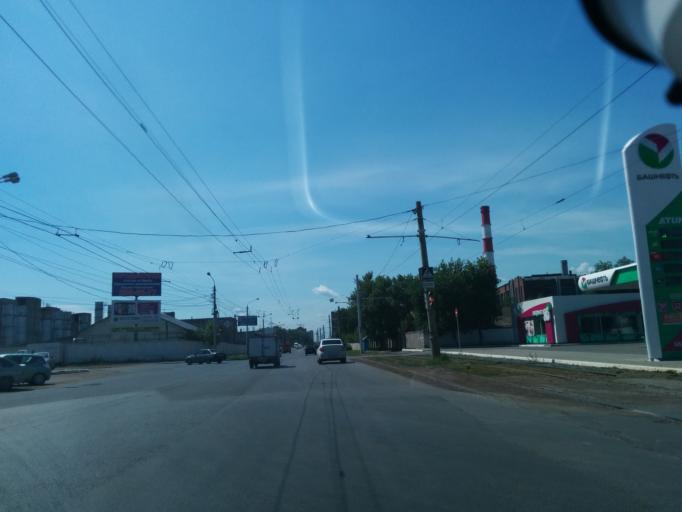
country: RU
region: Bashkortostan
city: Ufa
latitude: 54.7452
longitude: 55.9769
